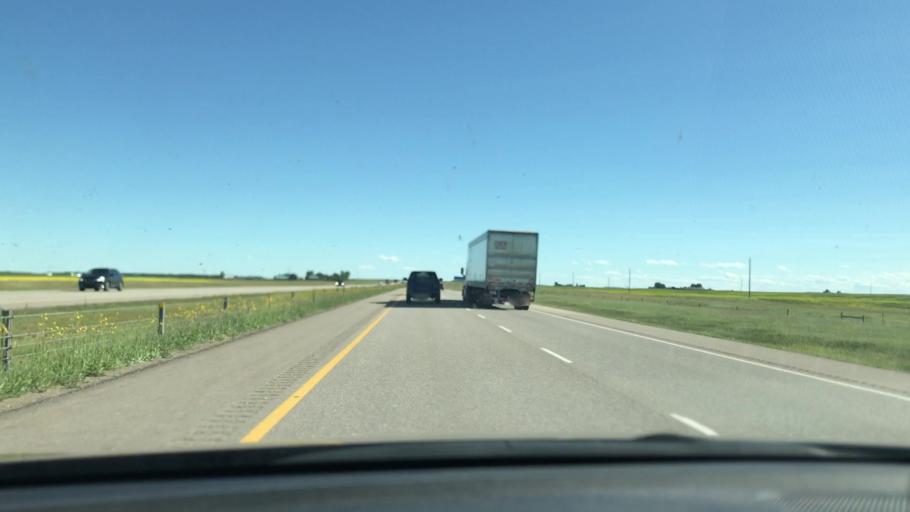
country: CA
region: Alberta
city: Didsbury
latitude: 51.6840
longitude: -114.0256
